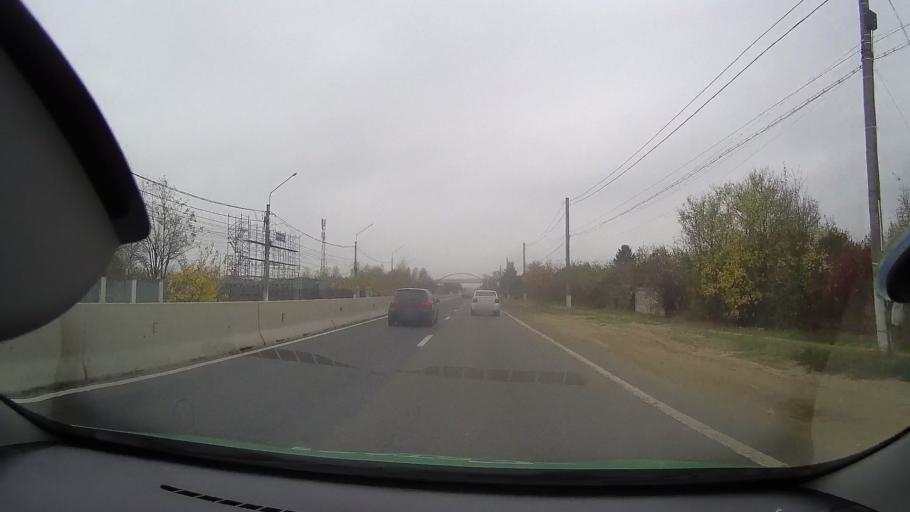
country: RO
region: Ilfov
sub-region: Comuna Corbeanca
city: Corbeanca
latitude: 44.6283
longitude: 26.0691
